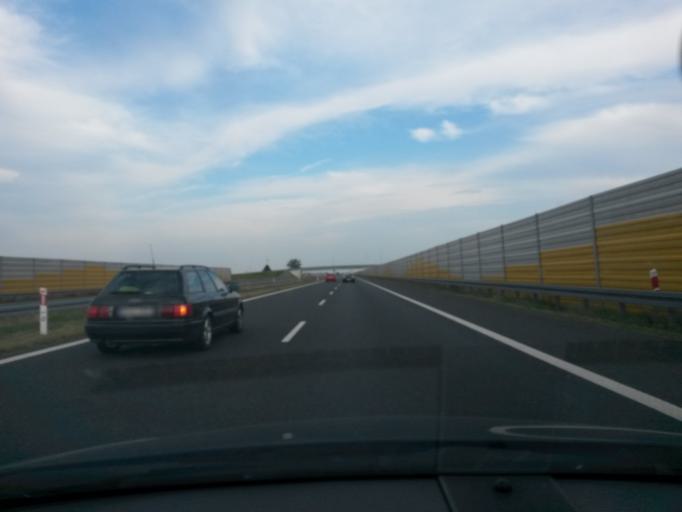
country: PL
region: Lodz Voivodeship
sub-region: Powiat leczycki
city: Swinice Warckie
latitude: 52.0206
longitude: 18.9324
